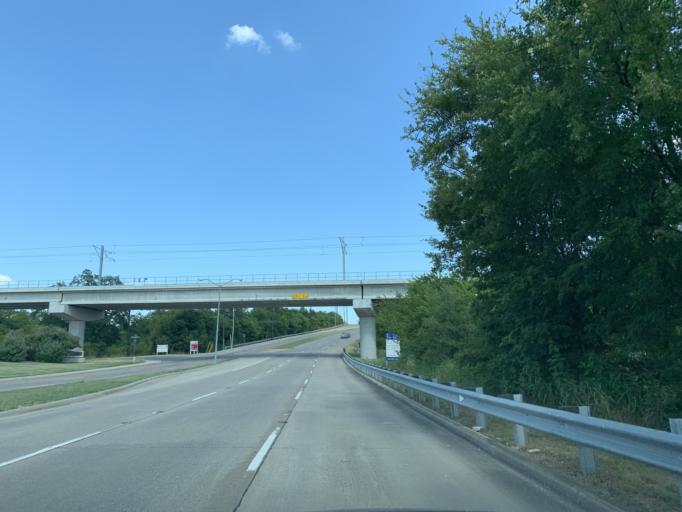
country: US
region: Texas
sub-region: Dallas County
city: Hutchins
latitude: 32.6629
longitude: -96.7884
